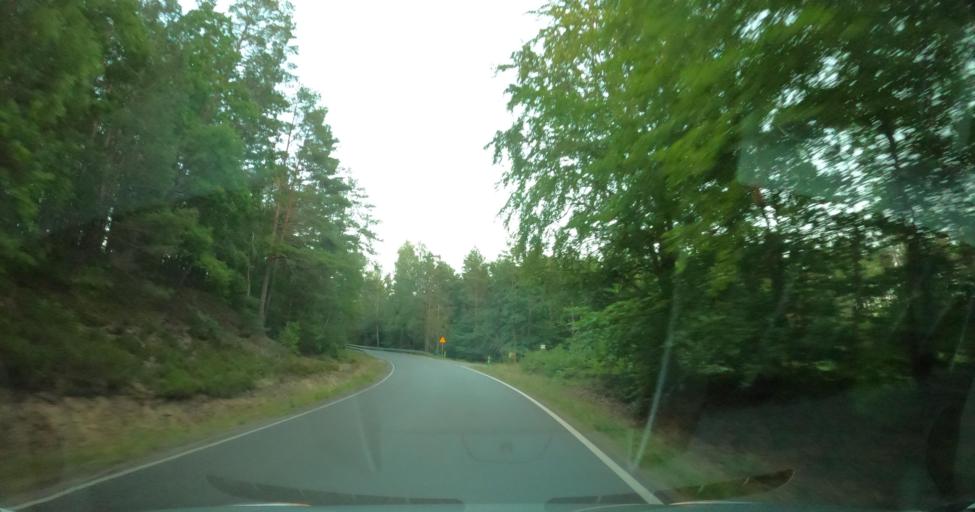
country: PL
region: Pomeranian Voivodeship
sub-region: Powiat leborski
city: Lebork
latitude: 54.5008
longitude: 17.8246
